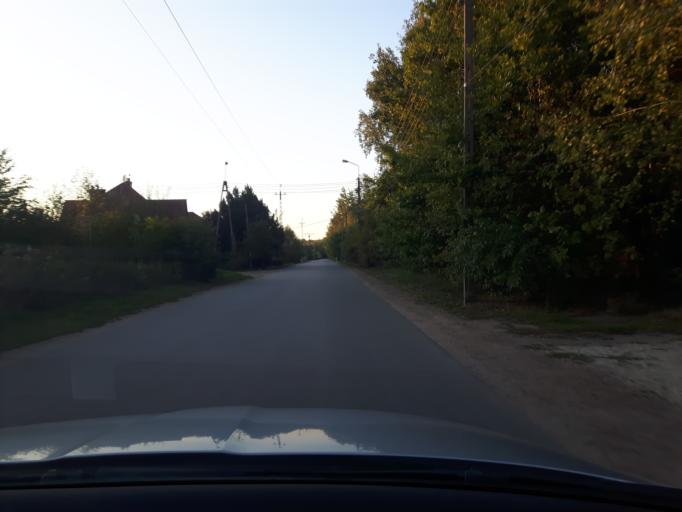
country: PL
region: Masovian Voivodeship
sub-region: Powiat wolominski
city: Kobylka
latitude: 52.3411
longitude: 21.1790
